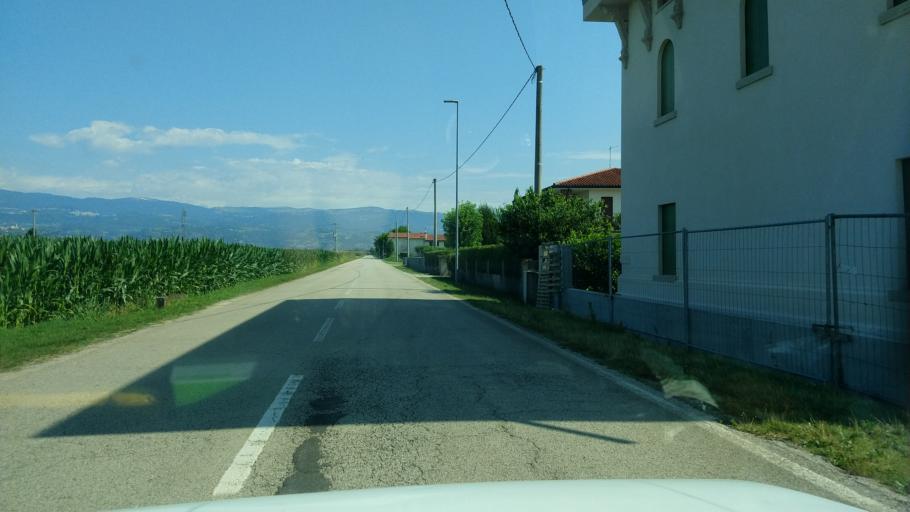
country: IT
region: Veneto
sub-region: Provincia di Vicenza
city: Sandrigo
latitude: 45.6722
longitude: 11.6082
